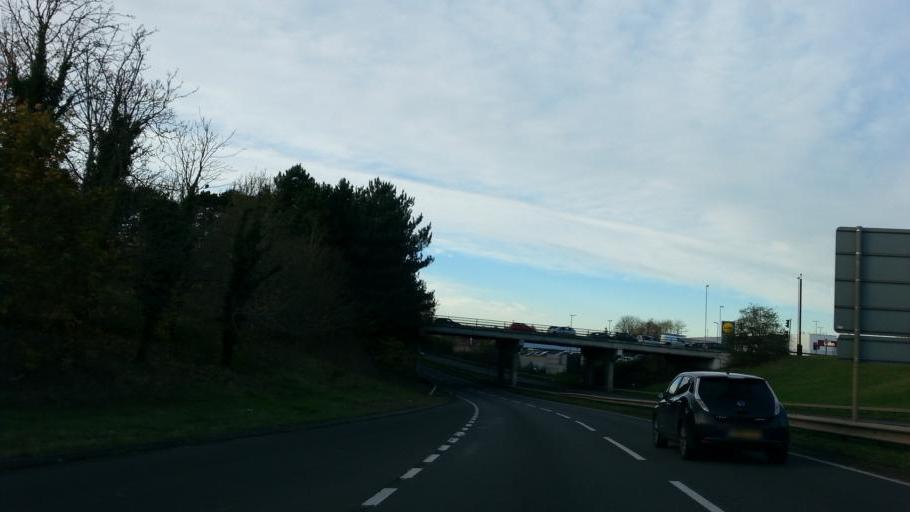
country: GB
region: England
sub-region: Northamptonshire
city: Northampton
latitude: 52.2535
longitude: -0.8351
